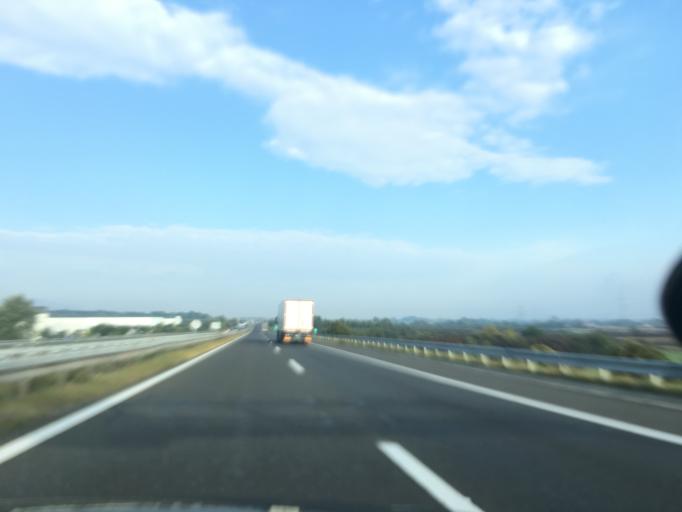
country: HR
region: Zagrebacka
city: Bestovje
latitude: 45.8025
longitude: 15.7785
